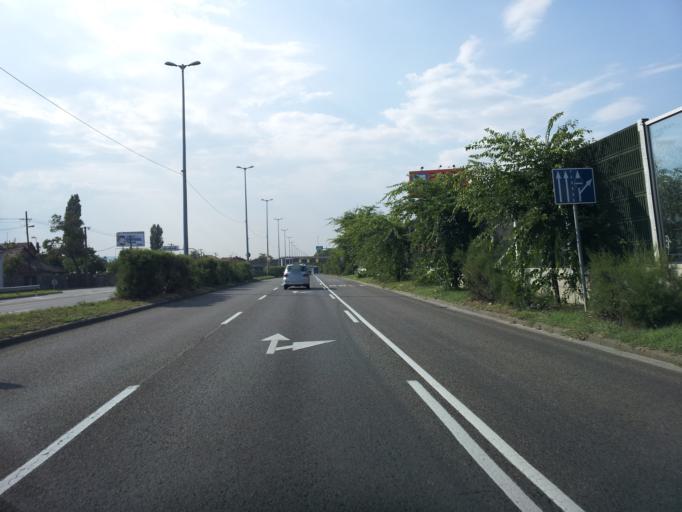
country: HU
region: Budapest
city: Budapest XIX. keruelet
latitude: 47.4446
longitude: 19.1293
